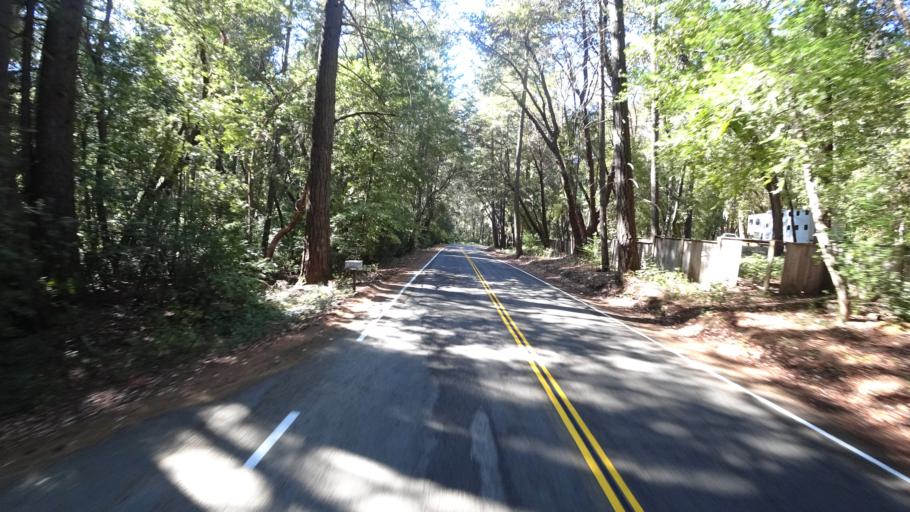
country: US
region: California
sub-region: Siskiyou County
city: Happy Camp
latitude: 41.3757
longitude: -123.4480
